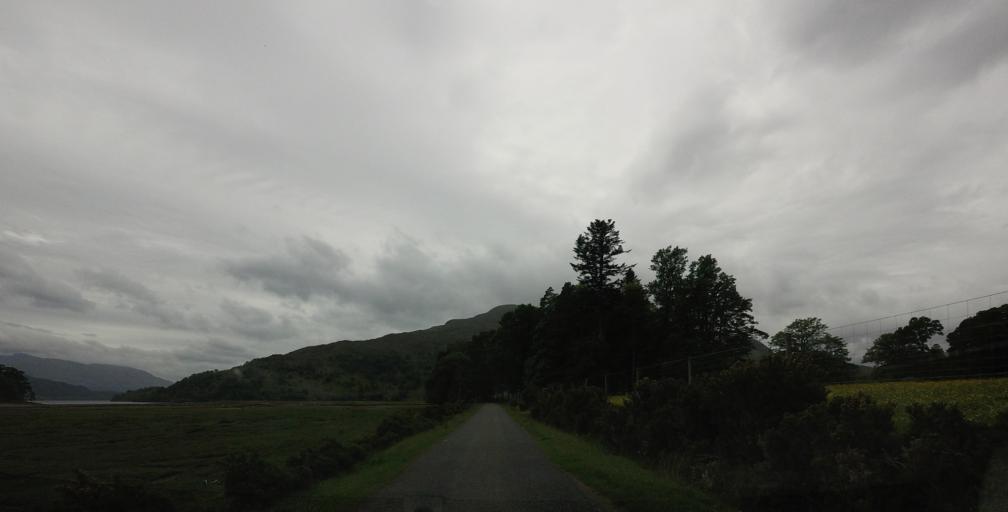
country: GB
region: Scotland
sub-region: Highland
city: Fort William
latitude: 56.7681
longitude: -5.2313
